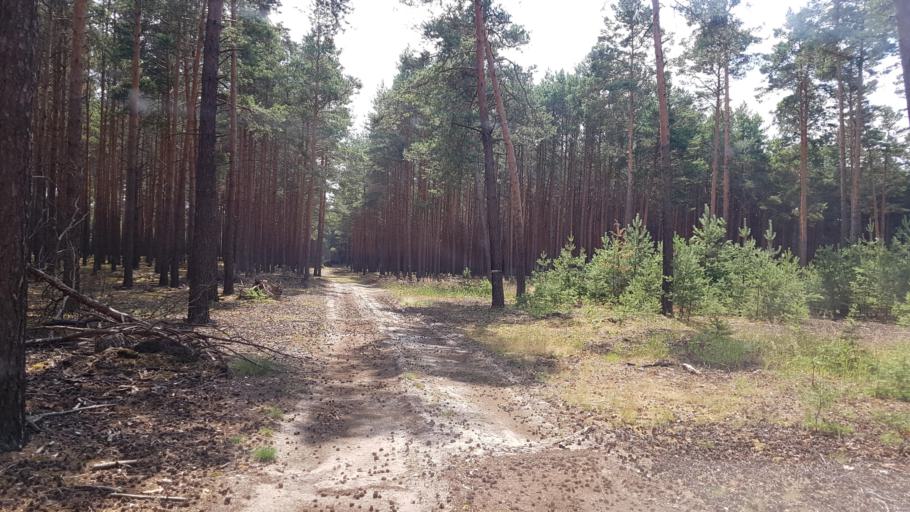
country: DE
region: Brandenburg
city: Crinitz
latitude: 51.6938
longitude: 13.8272
